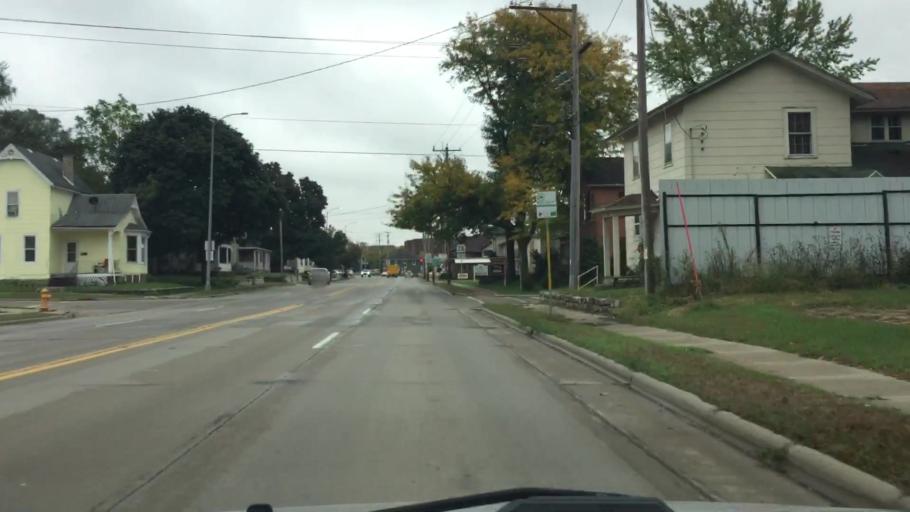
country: US
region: Wisconsin
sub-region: Rock County
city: Janesville
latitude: 42.6883
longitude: -89.0263
